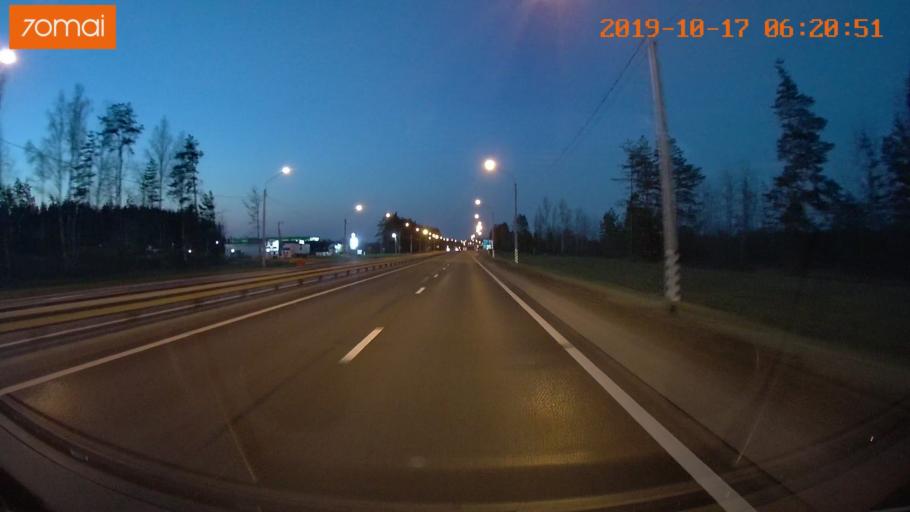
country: RU
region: Ivanovo
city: Lezhnevo
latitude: 56.8100
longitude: 40.8875
